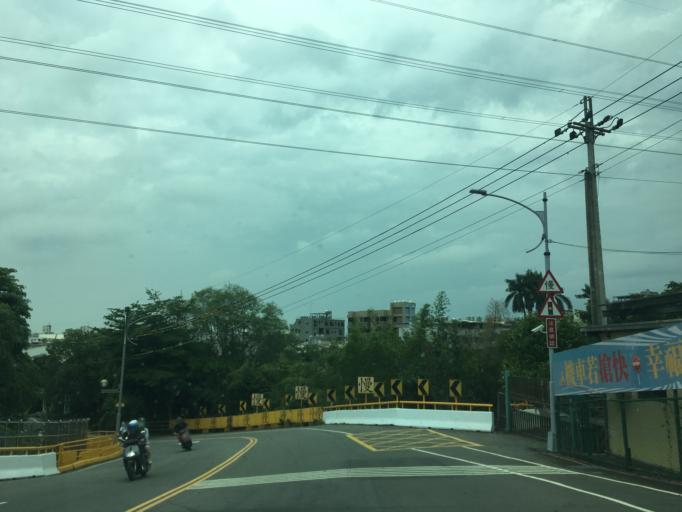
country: TW
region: Taiwan
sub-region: Taichung City
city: Taichung
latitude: 24.0716
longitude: 120.7158
